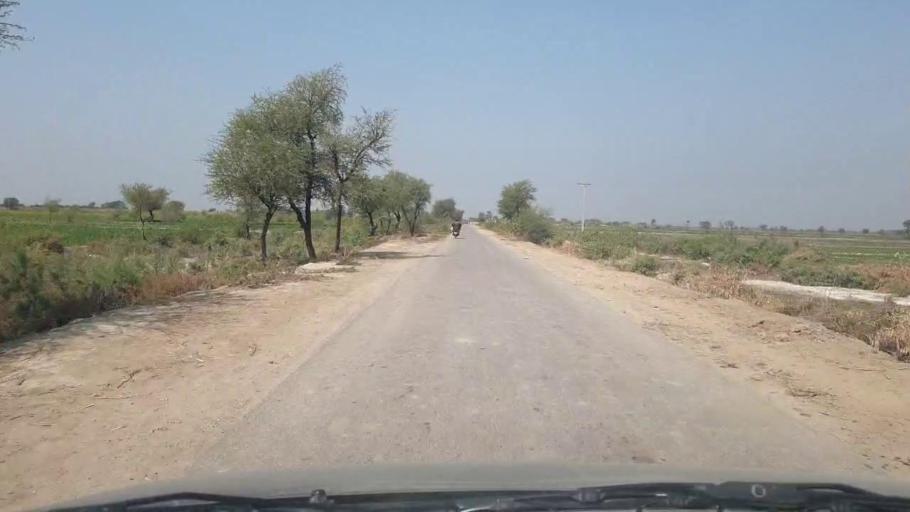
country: PK
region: Sindh
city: Mirwah Gorchani
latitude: 25.3239
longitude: 69.1507
